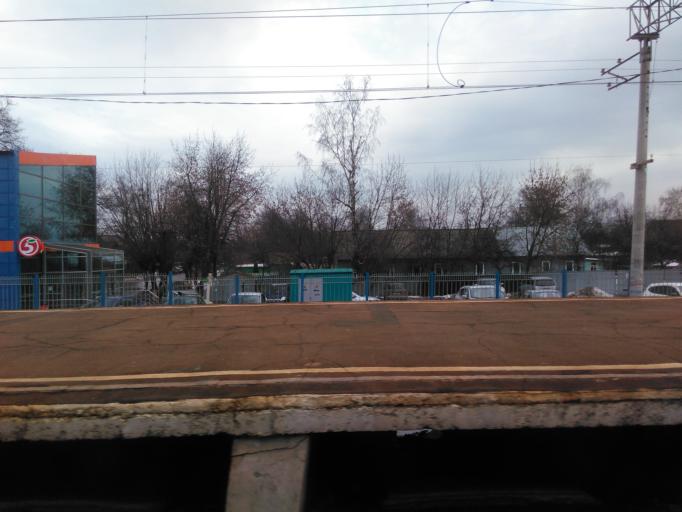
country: RU
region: Moskovskaya
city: Mamontovka
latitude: 55.9628
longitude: 37.8093
